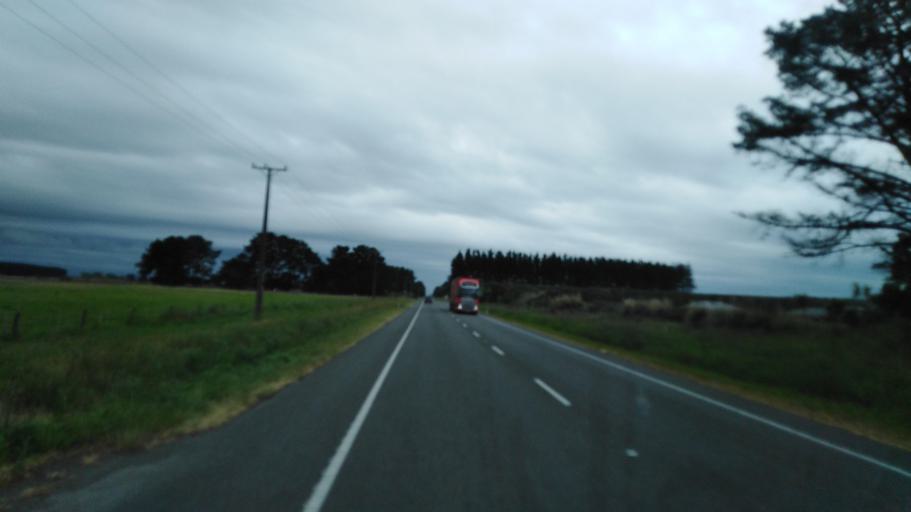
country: NZ
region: Manawatu-Wanganui
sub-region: Horowhenua District
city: Foxton
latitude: -40.4075
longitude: 175.3096
